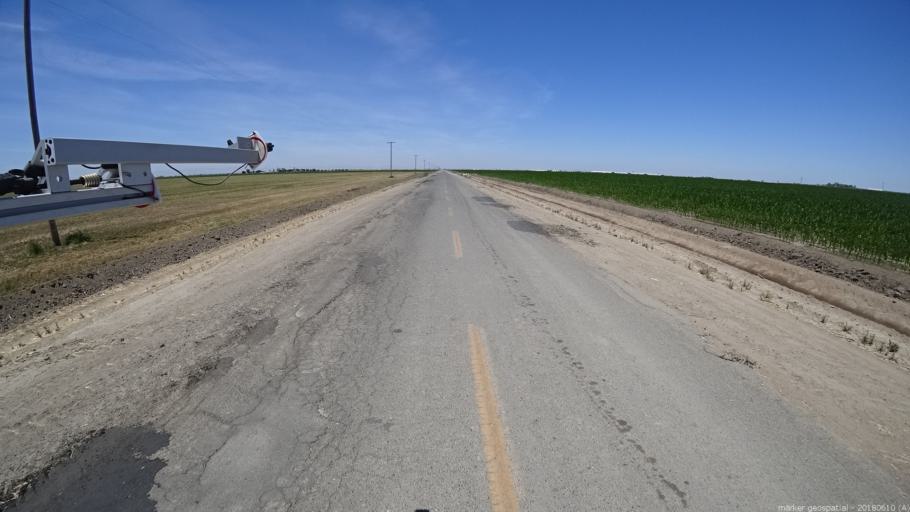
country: US
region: California
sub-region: Merced County
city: Dos Palos
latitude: 37.0546
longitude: -120.4561
